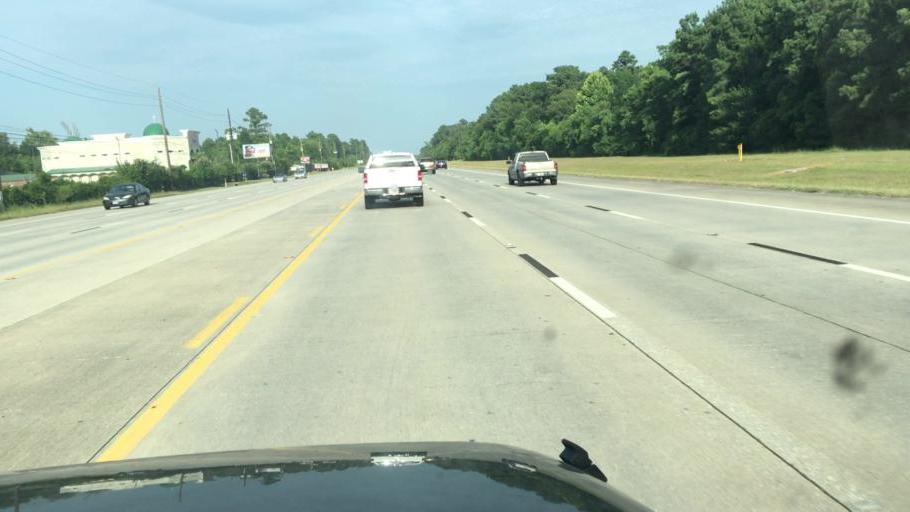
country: US
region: Texas
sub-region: Harris County
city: Humble
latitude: 30.0141
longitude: -95.3452
